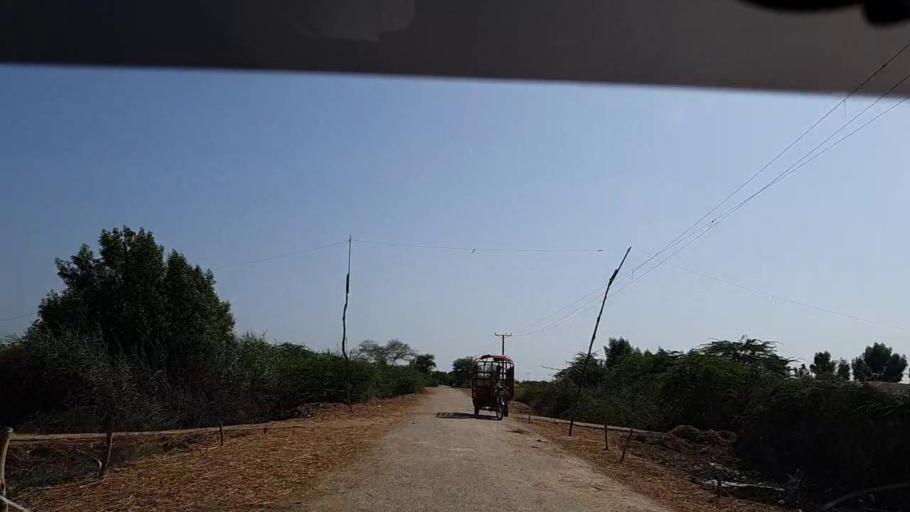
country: PK
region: Sindh
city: Badin
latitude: 24.6375
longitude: 68.7868
